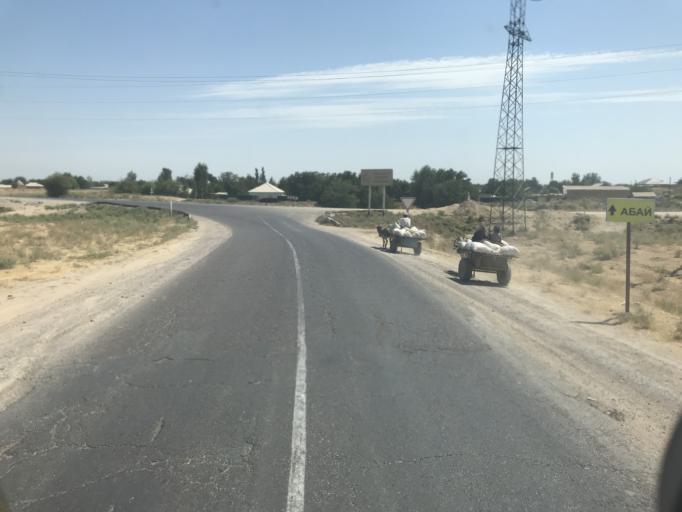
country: UZ
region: Toshkent
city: Yangiyul
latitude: 41.3283
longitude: 68.8926
